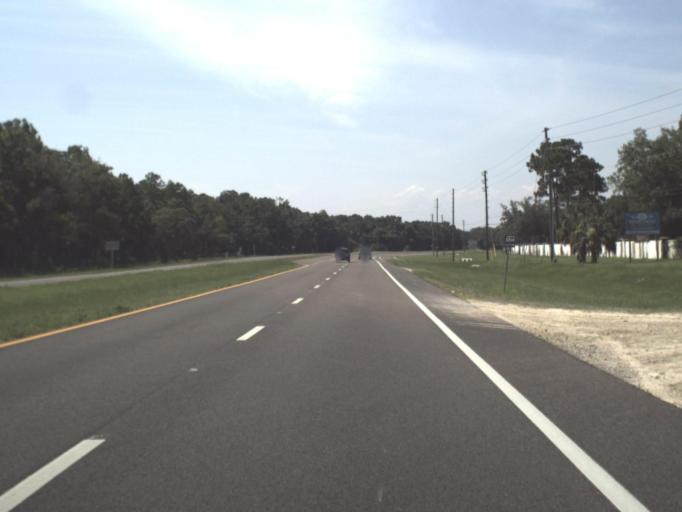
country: US
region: Florida
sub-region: Levy County
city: Inglis
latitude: 29.0176
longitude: -82.6666
